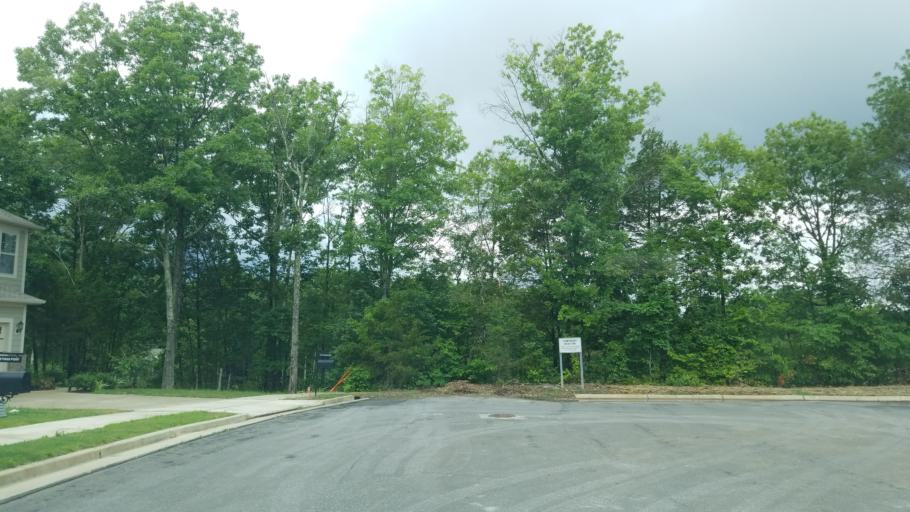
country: US
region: Tennessee
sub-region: Rutherford County
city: La Vergne
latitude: 36.0577
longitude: -86.6033
